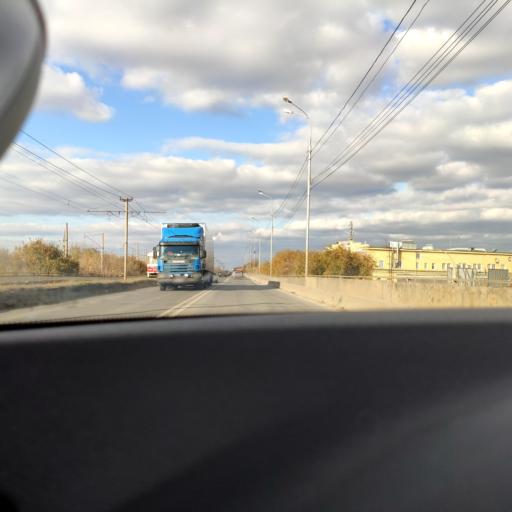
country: RU
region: Samara
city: Smyshlyayevka
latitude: 53.2182
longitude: 50.2906
